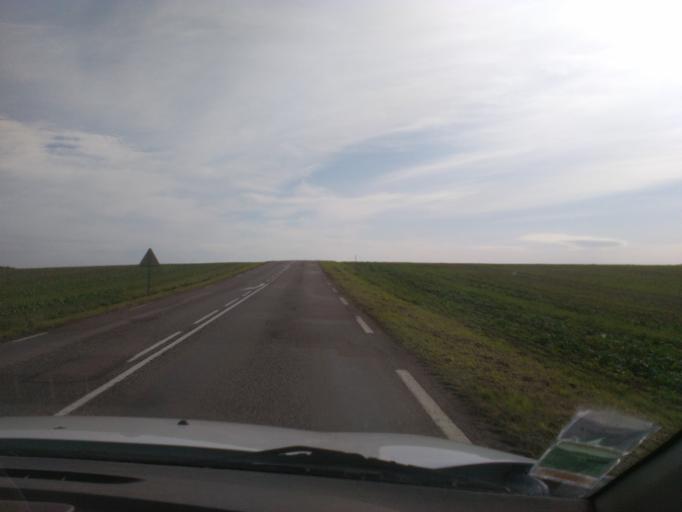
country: FR
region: Lorraine
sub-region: Departement des Vosges
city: Rambervillers
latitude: 48.3565
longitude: 6.5916
